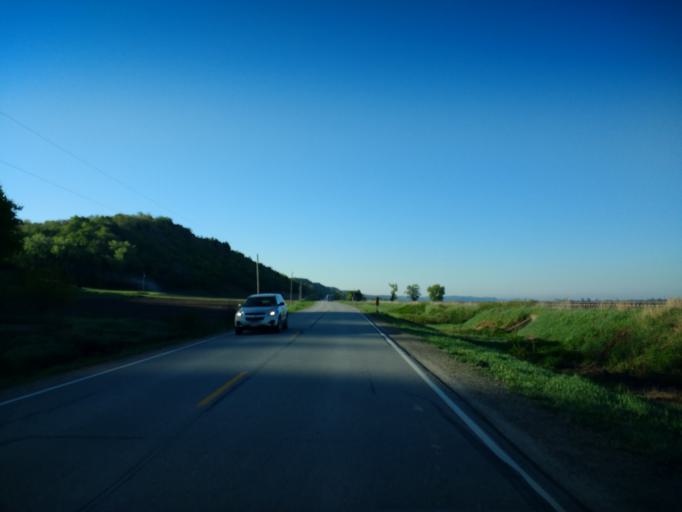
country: US
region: Iowa
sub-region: Harrison County
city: Missouri Valley
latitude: 41.4915
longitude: -95.8895
